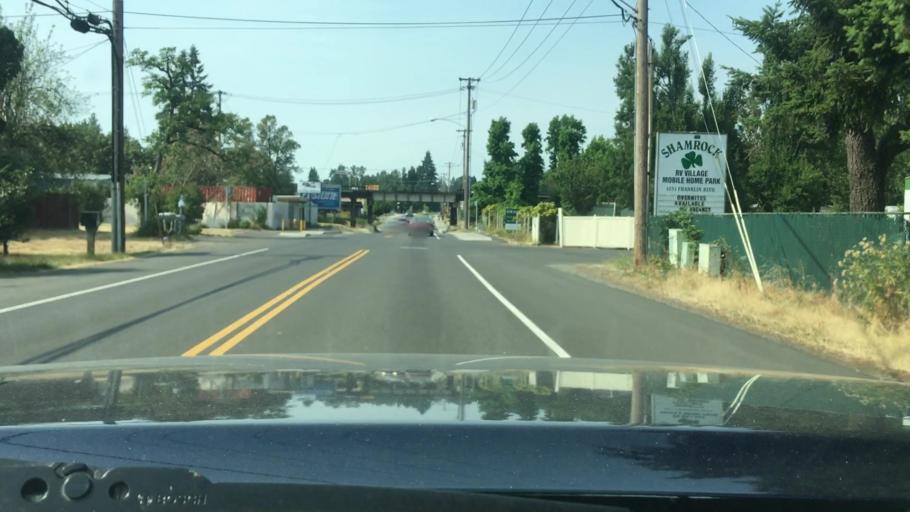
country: US
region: Oregon
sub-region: Lane County
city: Springfield
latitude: 44.0406
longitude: -123.0289
